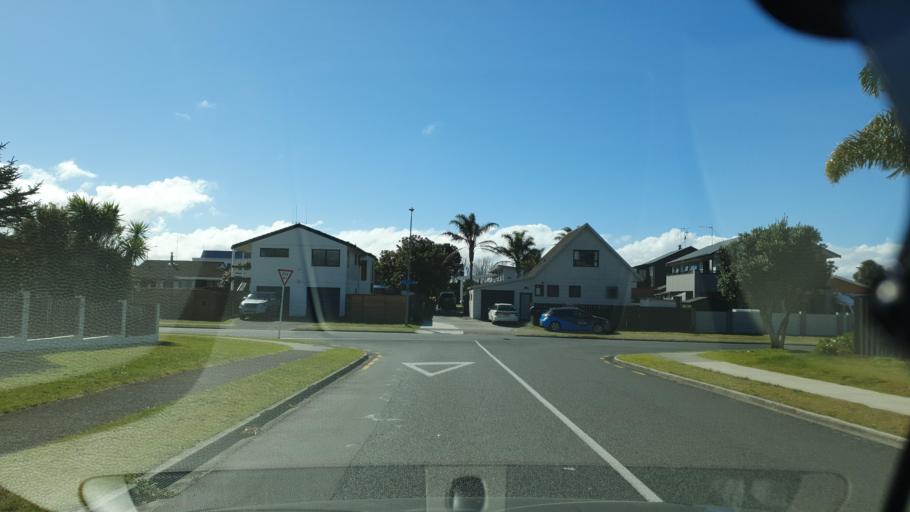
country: NZ
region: Bay of Plenty
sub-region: Tauranga City
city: Tauranga
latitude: -37.7024
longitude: 176.2938
